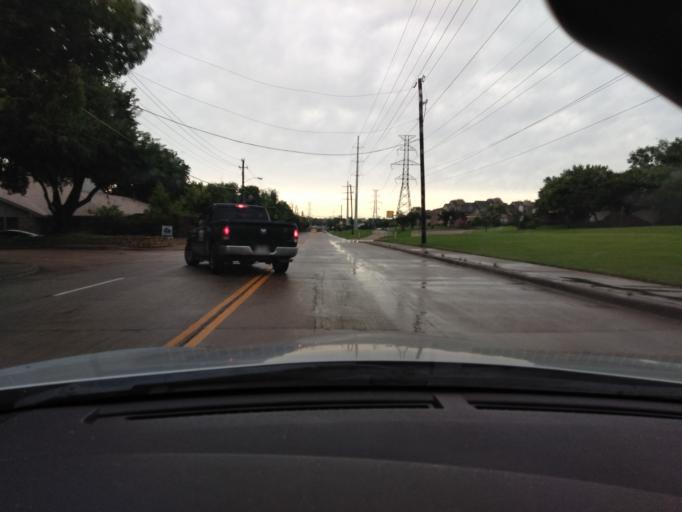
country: US
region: Texas
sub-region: Dallas County
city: Addison
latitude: 32.9850
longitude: -96.7786
